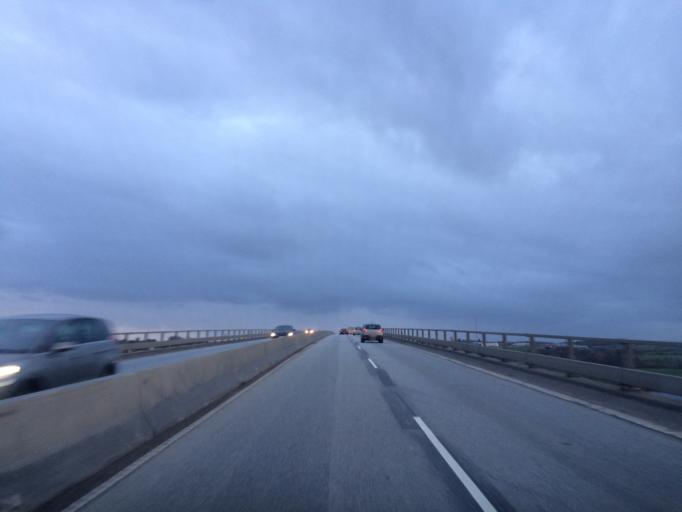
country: DK
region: South Denmark
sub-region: Sonderborg Kommune
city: Dybbol
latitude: 54.9227
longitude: 9.7710
